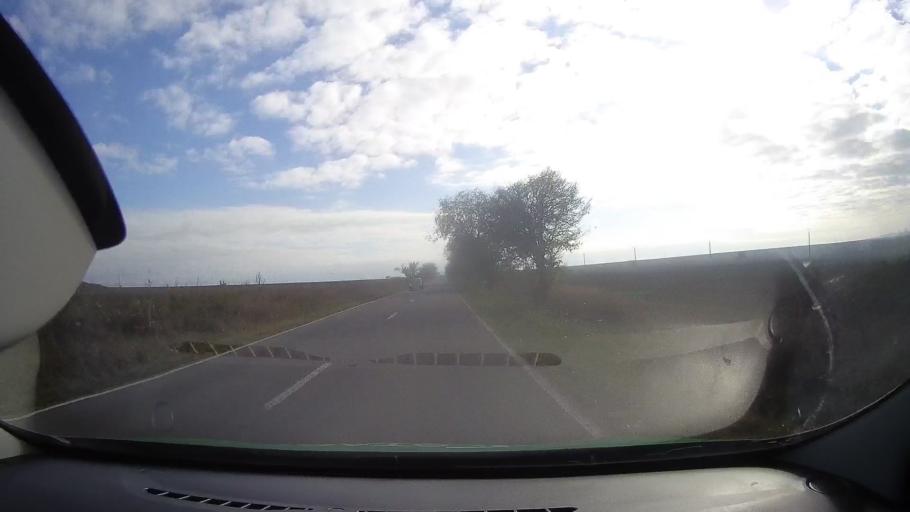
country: RO
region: Tulcea
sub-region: Comuna Bestepe
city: Bestepe
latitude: 45.0802
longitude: 29.0363
